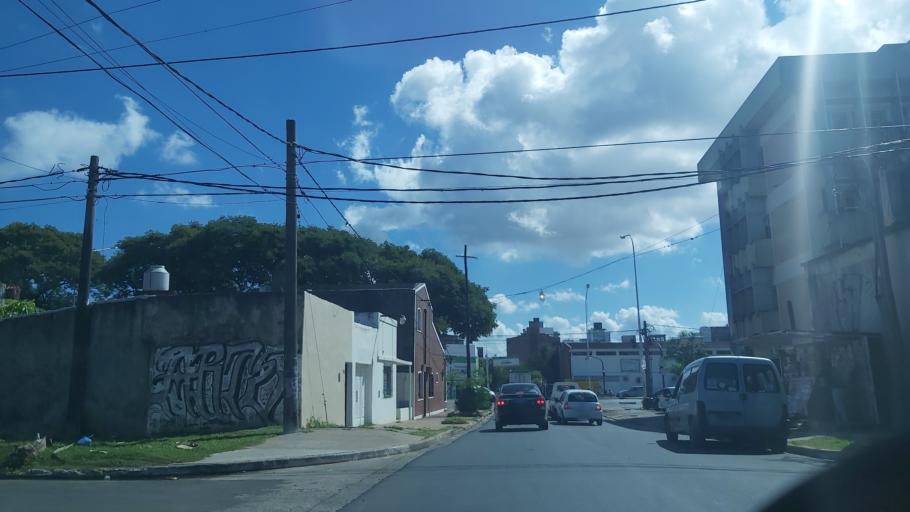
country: AR
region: Corrientes
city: Corrientes
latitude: -27.4765
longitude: -58.8366
